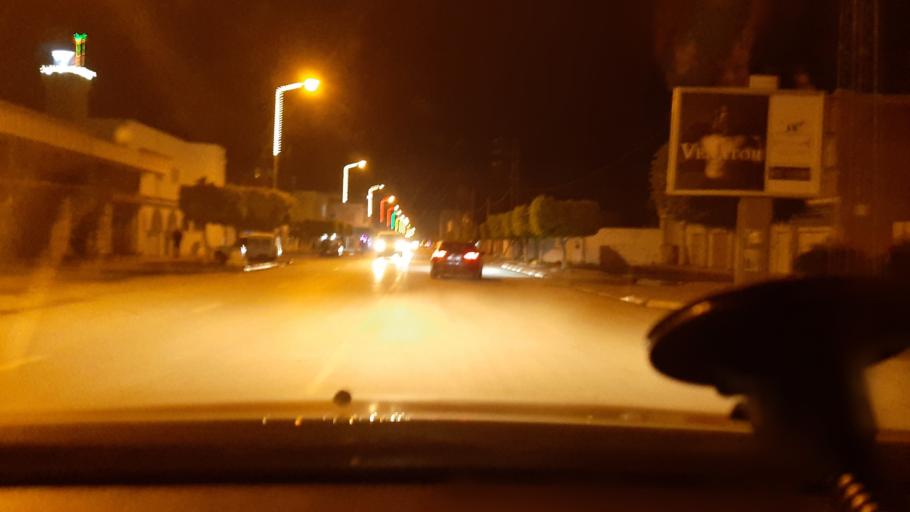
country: TN
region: Safaqis
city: Sfax
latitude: 34.7792
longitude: 10.7252
